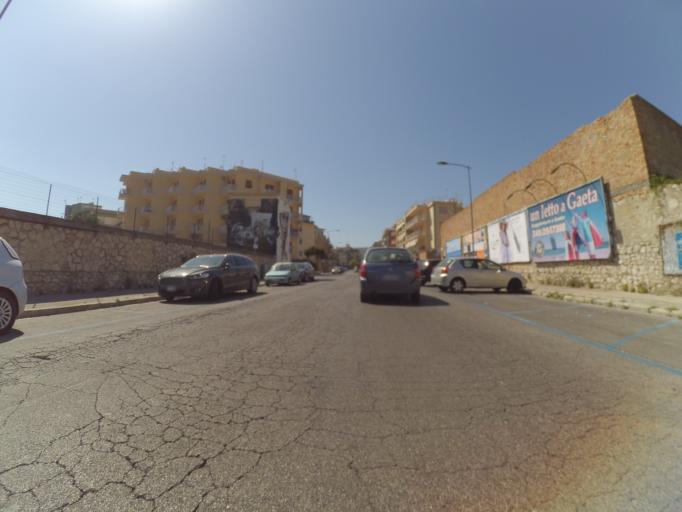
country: IT
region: Latium
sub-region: Provincia di Latina
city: Gaeta
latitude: 41.2123
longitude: 13.5665
